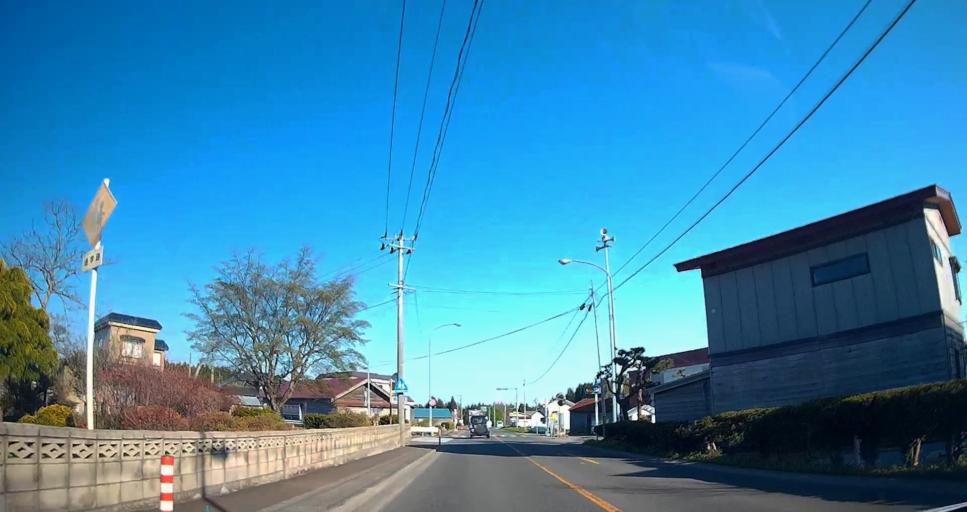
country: JP
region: Aomori
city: Mutsu
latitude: 41.3522
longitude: 141.2069
